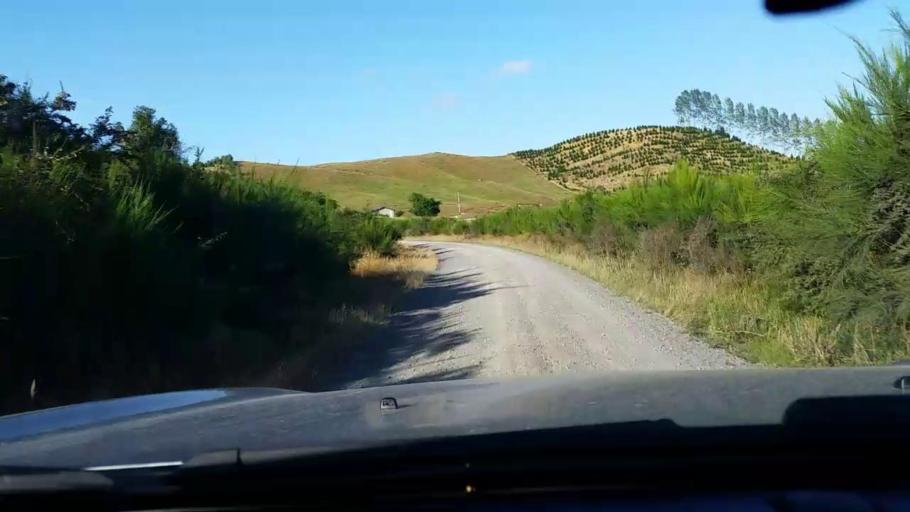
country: NZ
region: Waikato
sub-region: Taupo District
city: Taupo
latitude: -38.4972
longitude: 176.2039
